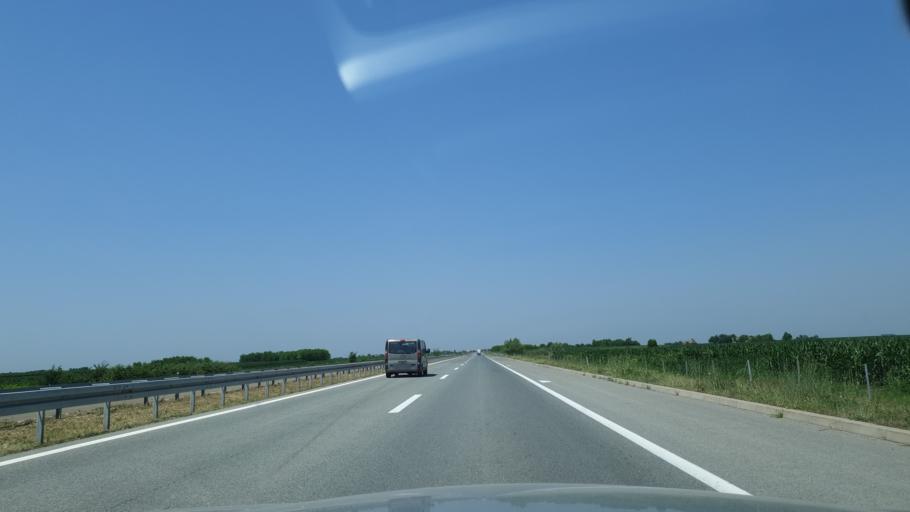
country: RS
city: Kisac
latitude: 45.3897
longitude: 19.7434
